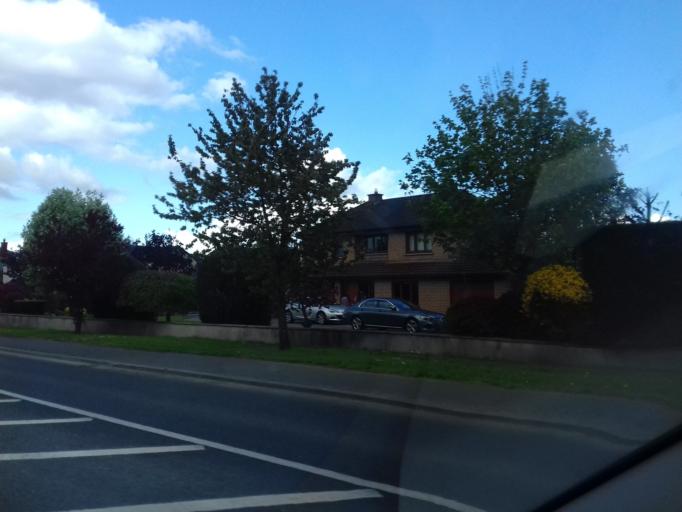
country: IE
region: Leinster
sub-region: Kilkenny
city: Kilkenny
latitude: 52.6341
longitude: -7.2520
